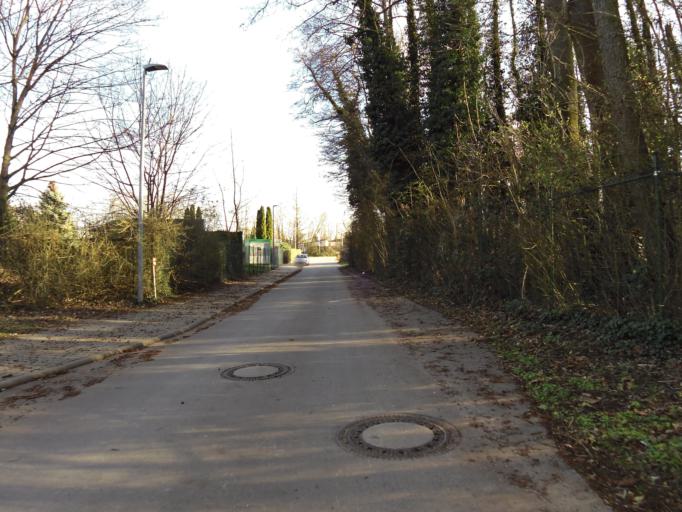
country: DE
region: Hesse
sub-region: Regierungsbezirk Darmstadt
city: Biblis
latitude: 49.6785
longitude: 8.4480
